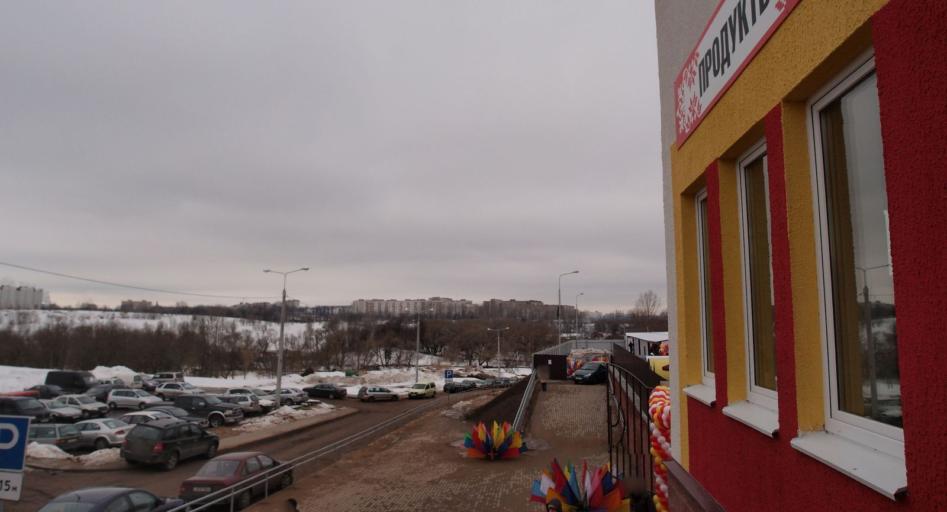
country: BY
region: Minsk
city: Syenitsa
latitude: 53.8551
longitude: 27.5682
